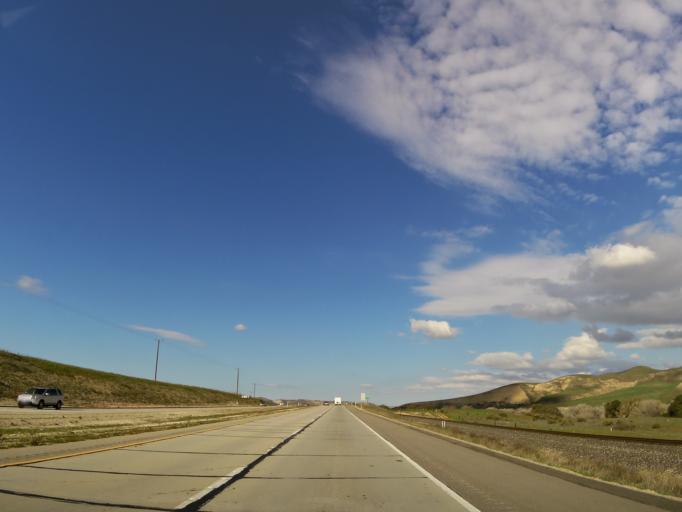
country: US
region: California
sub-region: San Luis Obispo County
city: San Miguel
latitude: 35.7899
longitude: -120.7305
